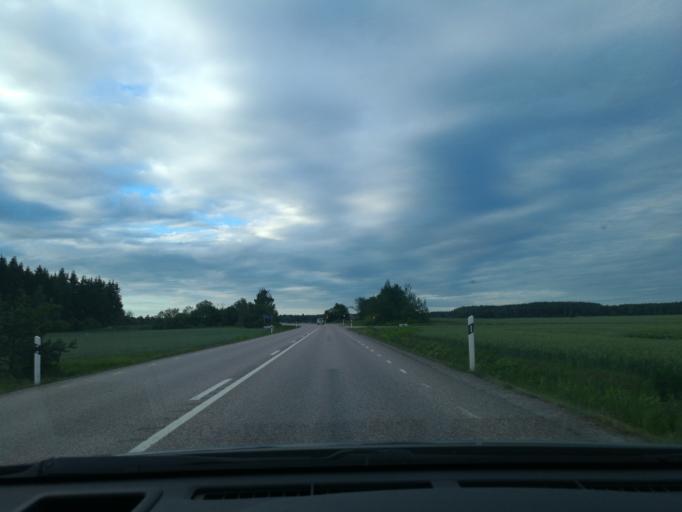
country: SE
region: Vaestmanland
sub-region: Hallstahammars Kommun
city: Kolback
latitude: 59.5504
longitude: 16.3349
